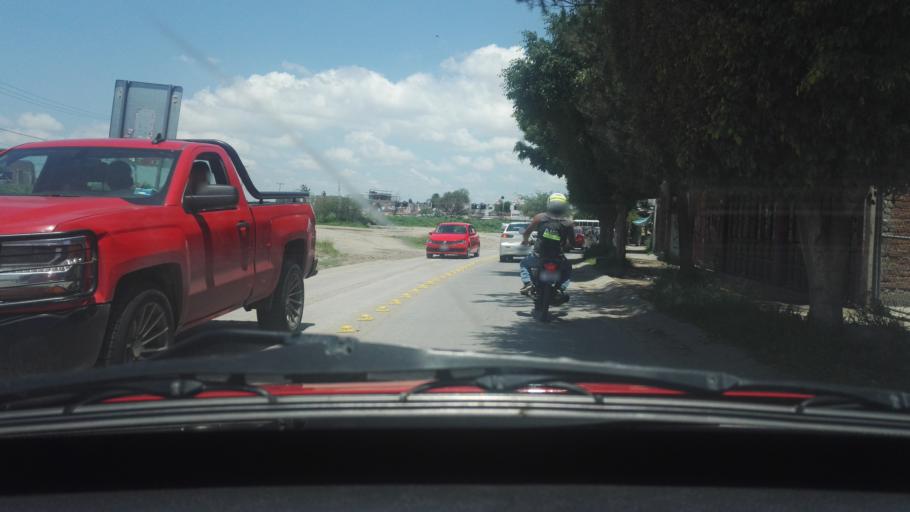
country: MX
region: Guanajuato
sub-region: Leon
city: San Jose de Duran (Los Troncoso)
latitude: 21.0771
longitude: -101.6367
